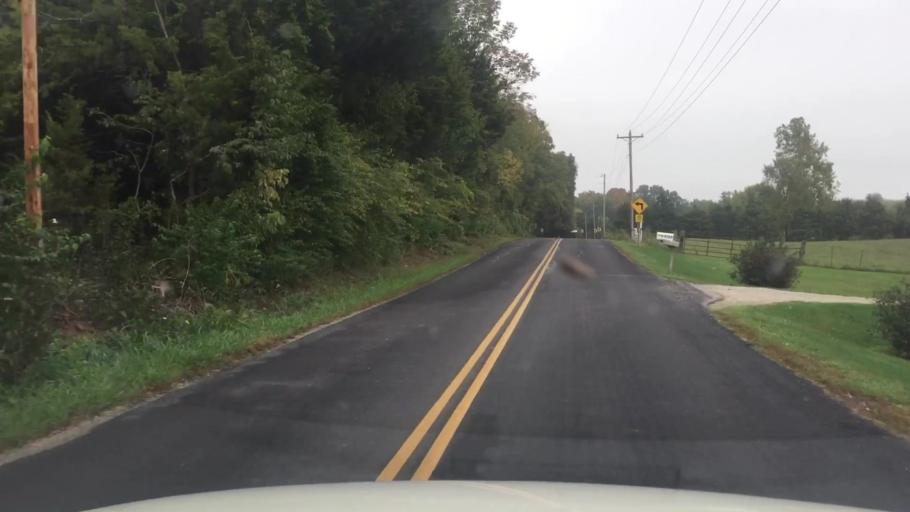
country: US
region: Missouri
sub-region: Boone County
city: Ashland
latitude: 38.8171
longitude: -92.2928
